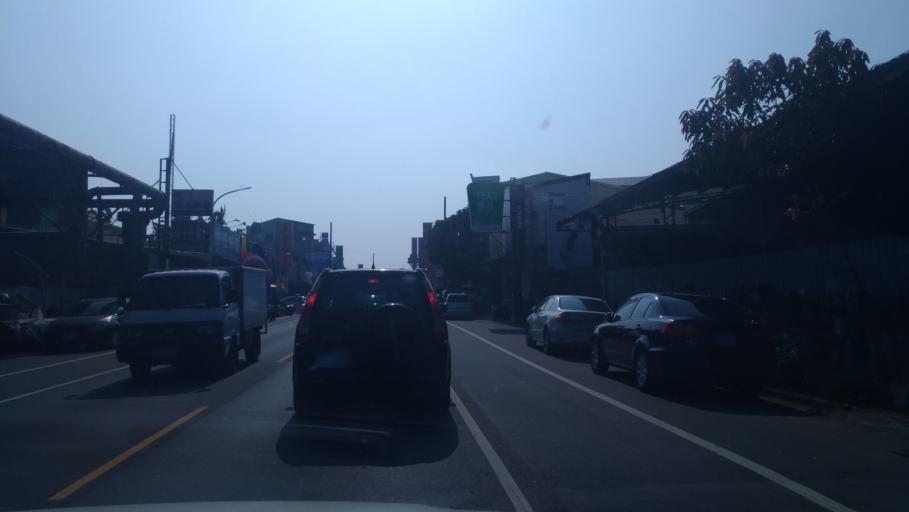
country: TW
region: Taiwan
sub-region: Chiayi
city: Jiayi Shi
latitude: 23.5040
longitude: 120.4385
